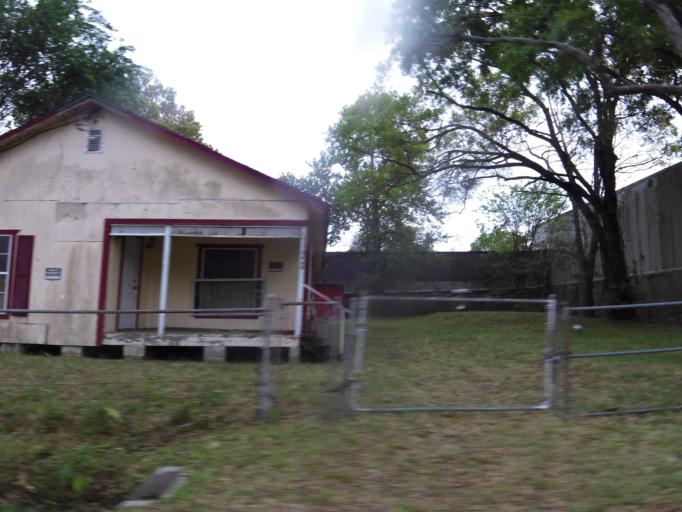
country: US
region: Florida
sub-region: Duval County
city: Jacksonville
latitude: 30.3232
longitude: -81.7258
